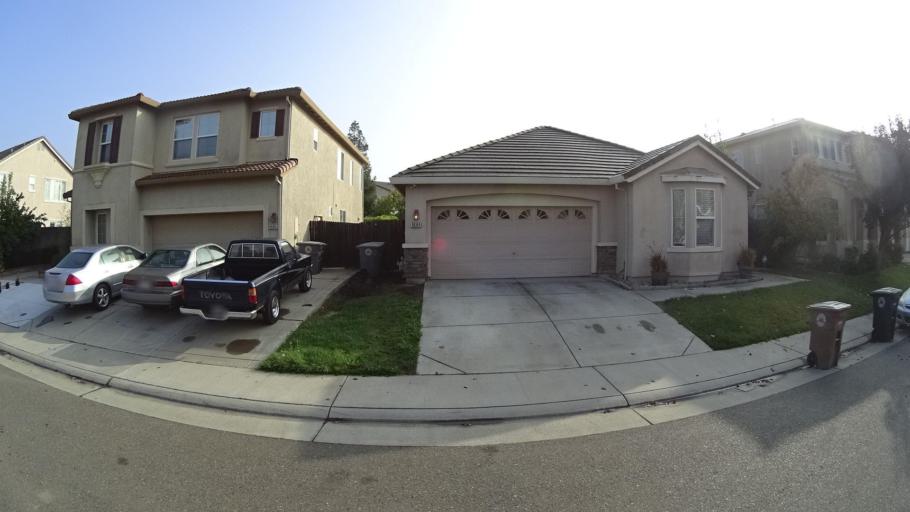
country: US
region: California
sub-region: Sacramento County
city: Elk Grove
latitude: 38.4048
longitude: -121.3525
